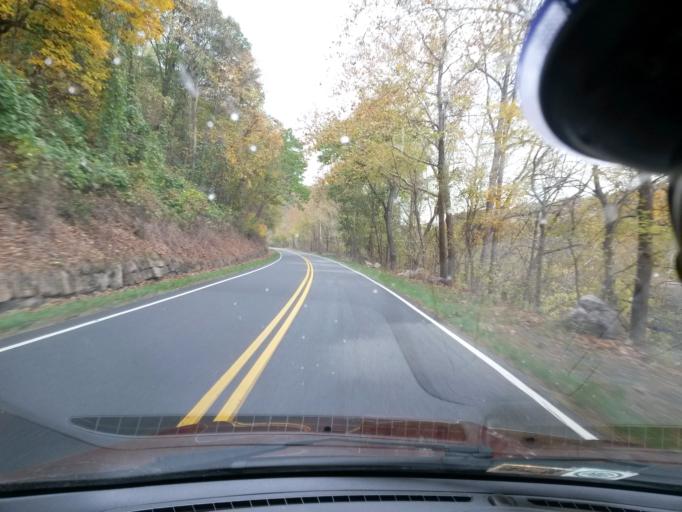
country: US
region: Virginia
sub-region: Alleghany County
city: Clifton Forge
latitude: 37.8133
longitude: -79.8050
